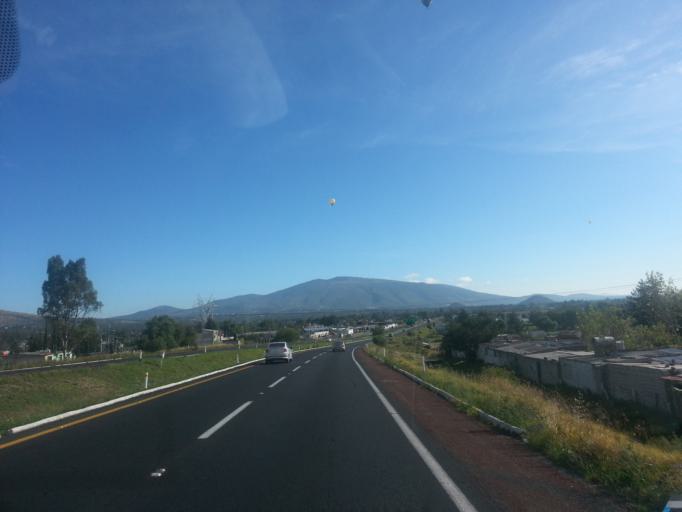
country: MX
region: Morelos
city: Teotihuacan de Arista
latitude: 19.6676
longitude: -98.8691
